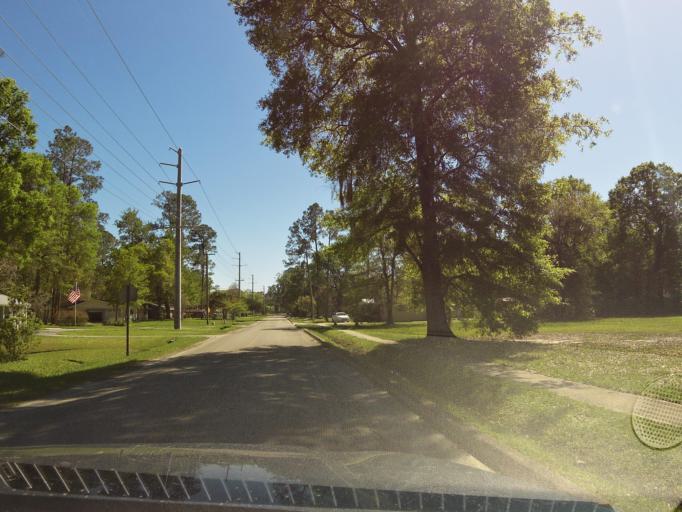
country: US
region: Florida
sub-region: Bradford County
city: Starke
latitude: 29.9348
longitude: -82.1024
